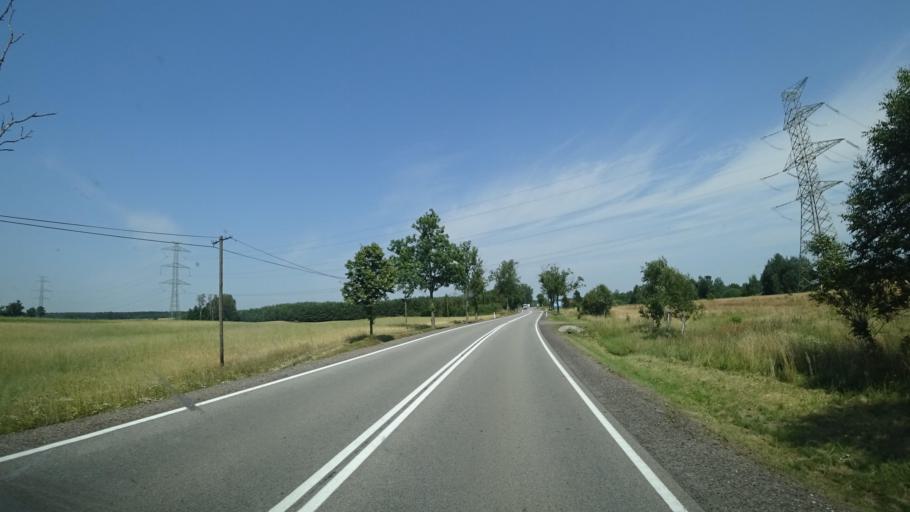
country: PL
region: Pomeranian Voivodeship
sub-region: Powiat koscierski
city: Koscierzyna
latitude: 54.1543
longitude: 18.0314
